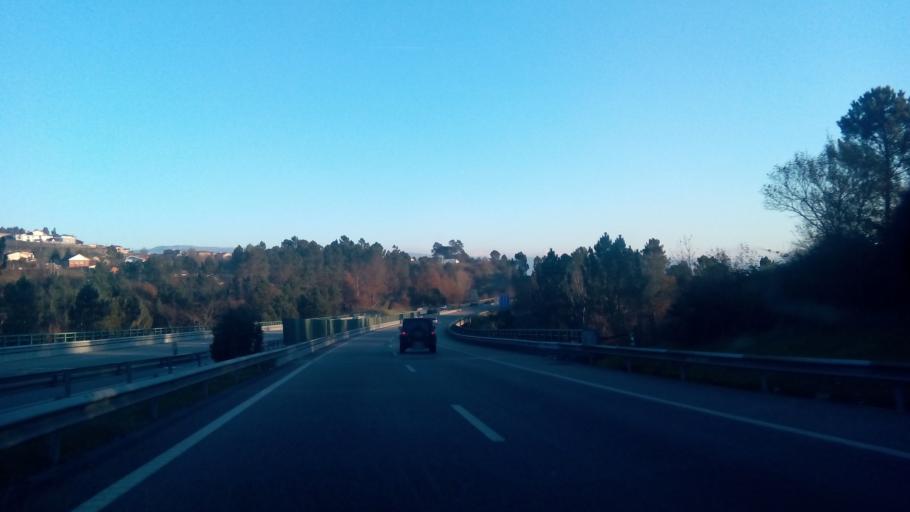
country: PT
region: Porto
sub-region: Marco de Canaveses
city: Marco de Canavezes
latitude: 41.2258
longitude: -8.1719
